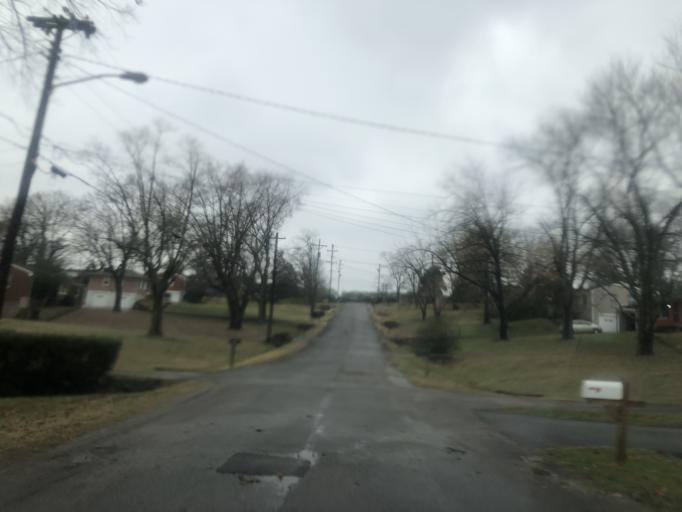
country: US
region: Tennessee
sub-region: Davidson County
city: Lakewood
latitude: 36.1513
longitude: -86.6610
